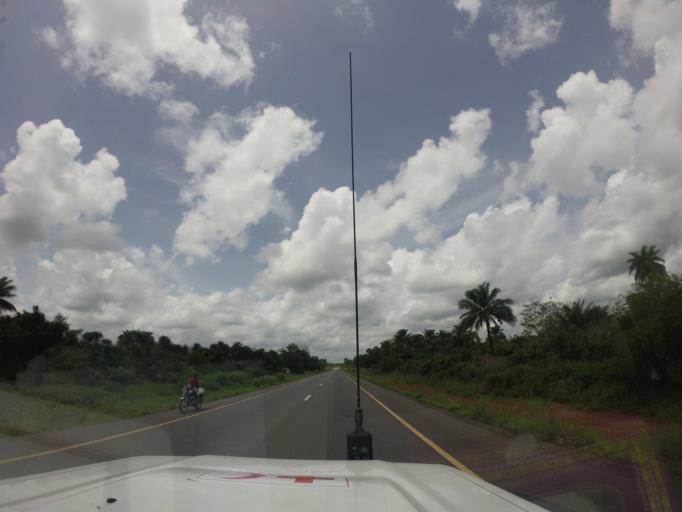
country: SL
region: Northern Province
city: Kambia
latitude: 9.0249
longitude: -12.8922
